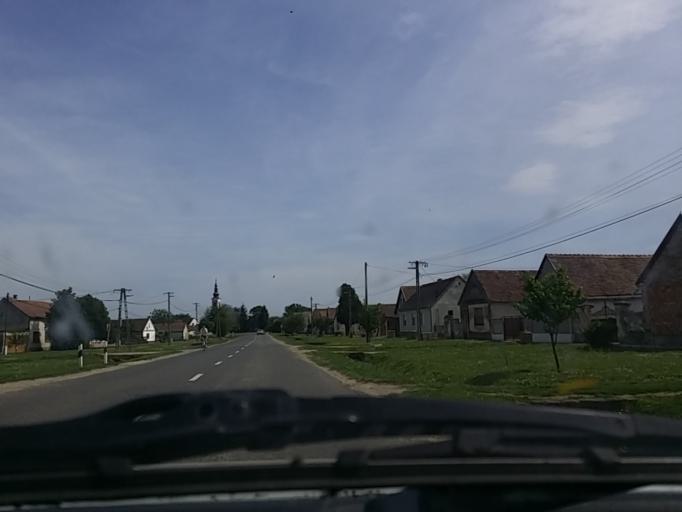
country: HU
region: Baranya
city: Harkany
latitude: 45.8376
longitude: 18.1605
